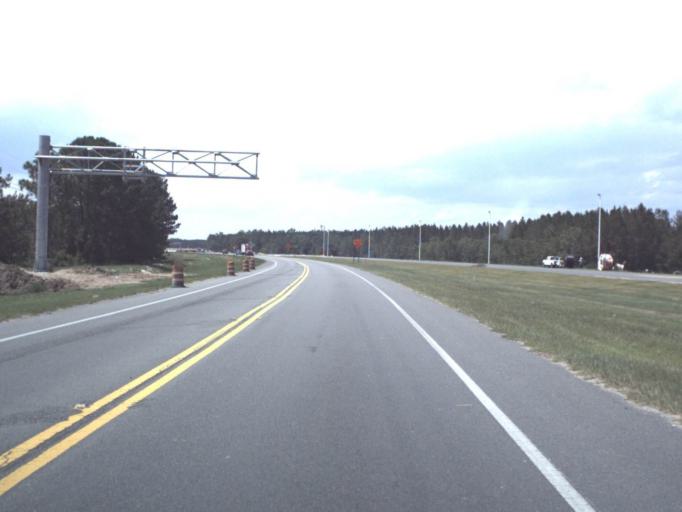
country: US
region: Florida
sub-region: Clay County
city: Lakeside
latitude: 30.1745
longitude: -81.8316
